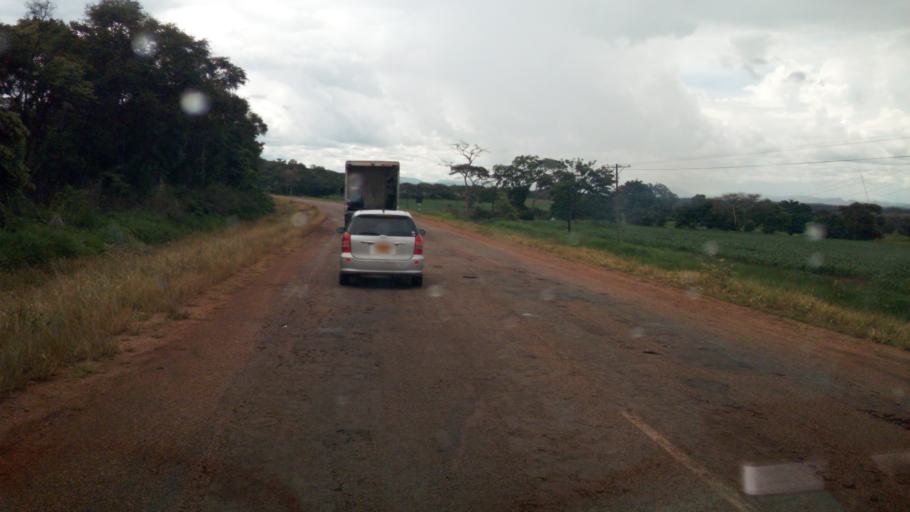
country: ZW
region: Mashonaland Central
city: Glendale
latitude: -17.3302
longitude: 31.1472
